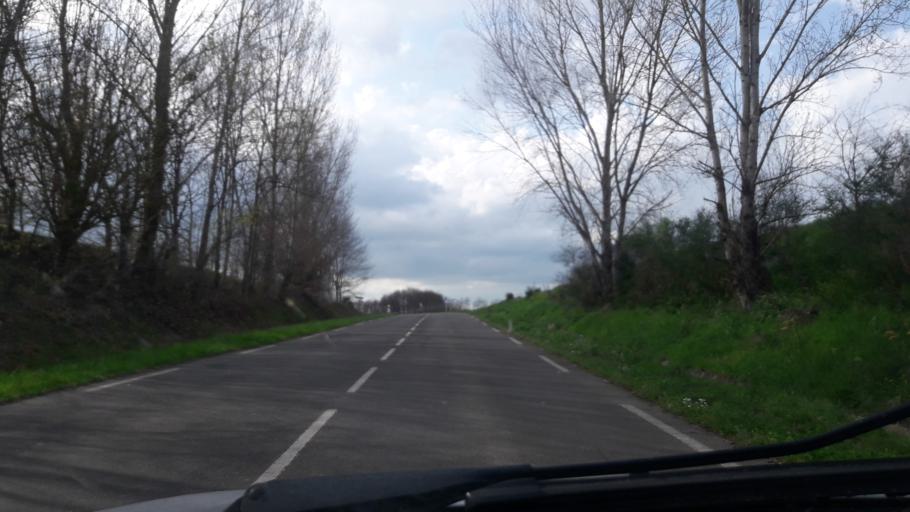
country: FR
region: Midi-Pyrenees
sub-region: Departement de la Haute-Garonne
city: Rieux-Volvestre
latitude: 43.2664
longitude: 1.2021
